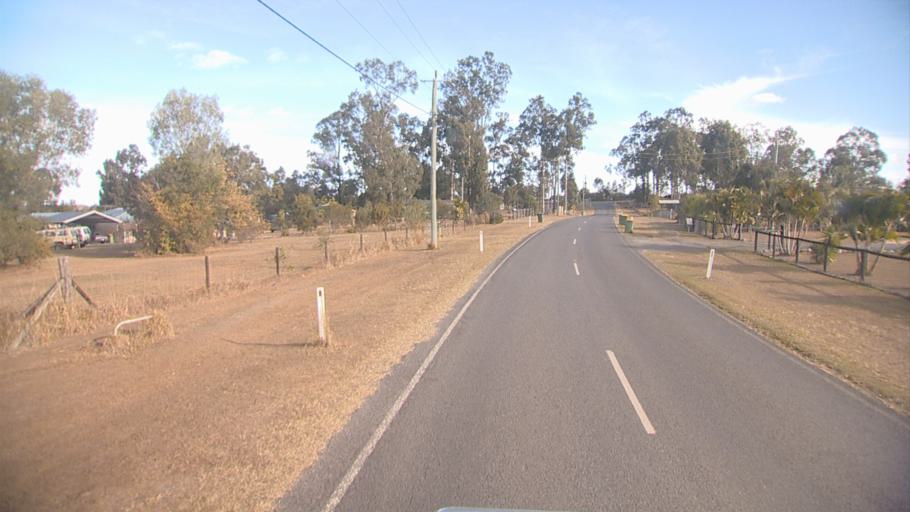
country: AU
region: Queensland
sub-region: Logan
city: Cedar Vale
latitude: -27.8662
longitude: 153.0054
